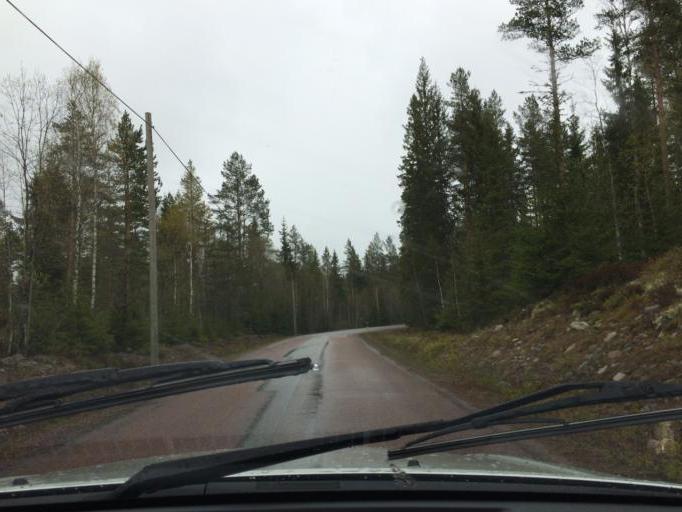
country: SE
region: Dalarna
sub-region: Ludvika Kommun
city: Abborrberget
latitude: 60.0449
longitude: 14.7379
